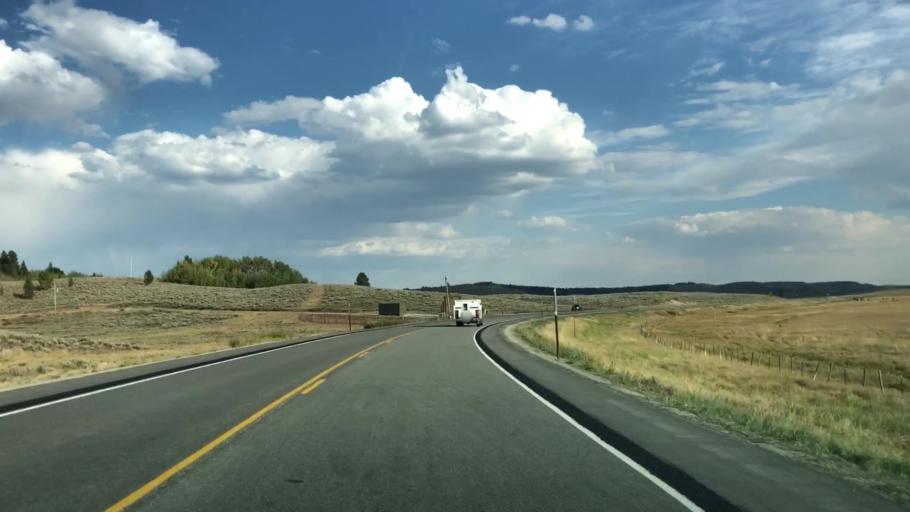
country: US
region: Wyoming
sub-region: Sublette County
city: Pinedale
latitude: 43.1313
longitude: -110.1930
